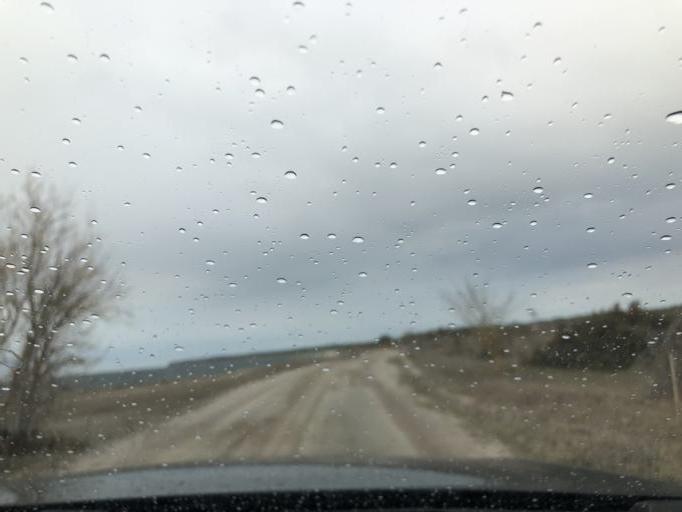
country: SE
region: Kalmar
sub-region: Borgholms Kommun
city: Borgholm
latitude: 57.2200
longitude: 16.9504
